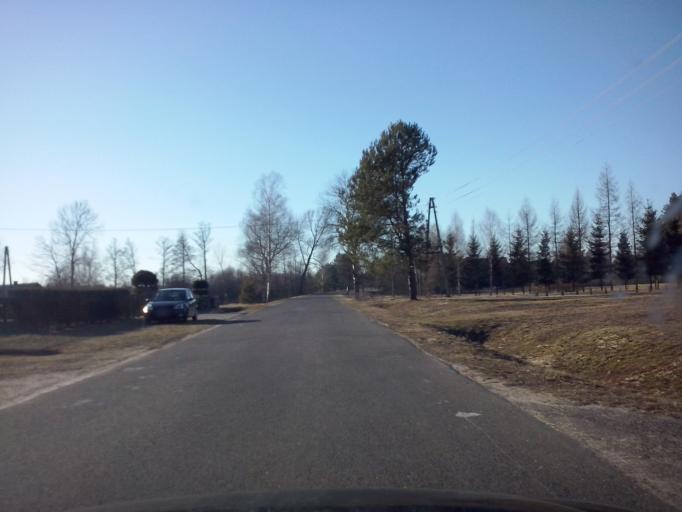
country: PL
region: Subcarpathian Voivodeship
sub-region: Powiat nizanski
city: Harasiuki
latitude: 50.4801
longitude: 22.5058
